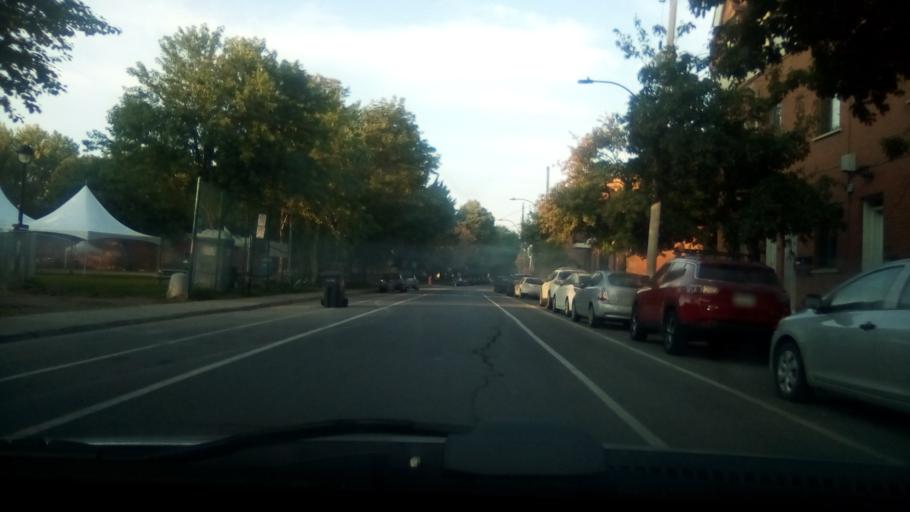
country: CA
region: Quebec
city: Westmount
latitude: 45.4792
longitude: -73.5648
